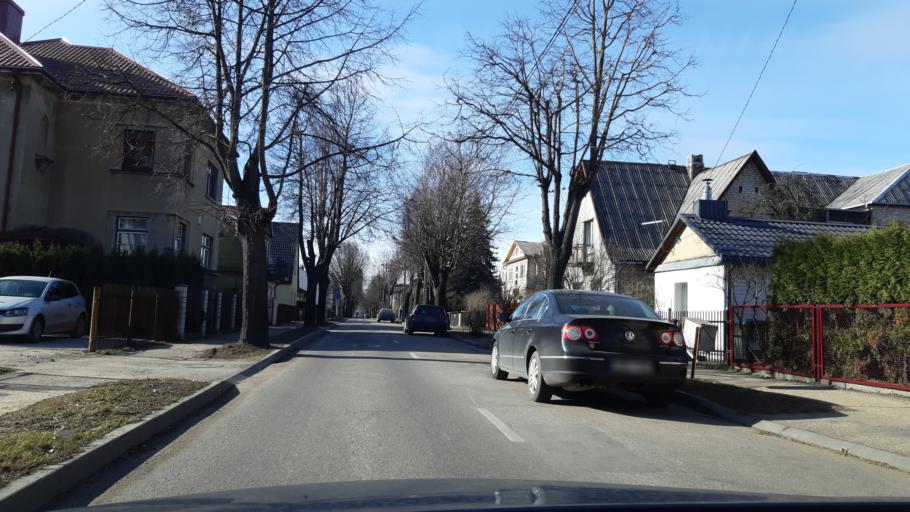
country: LT
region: Kauno apskritis
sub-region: Kaunas
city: Eiguliai
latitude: 54.9074
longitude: 23.9300
